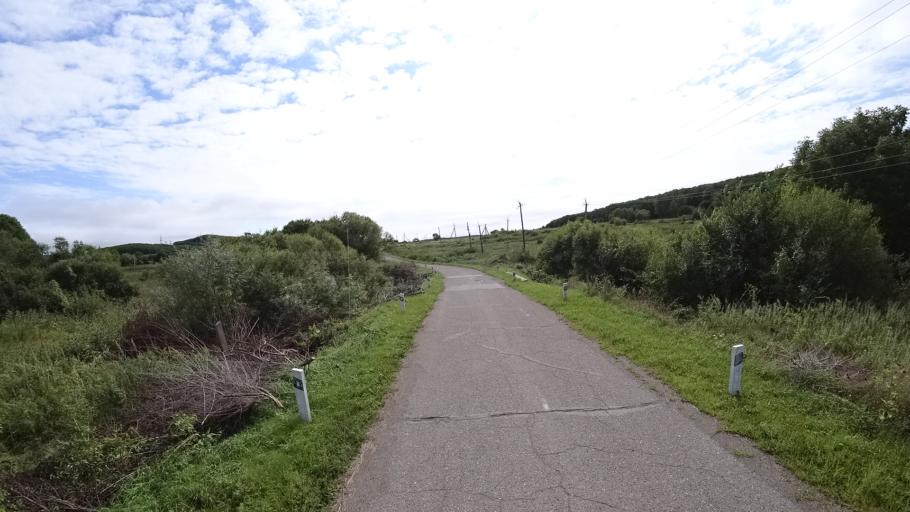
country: RU
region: Primorskiy
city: Lyalichi
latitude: 44.1363
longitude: 132.3875
